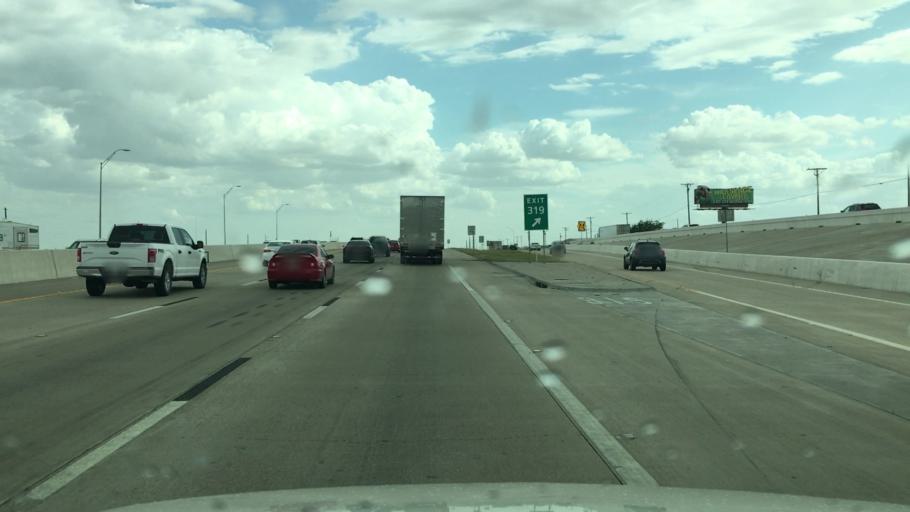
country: US
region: Texas
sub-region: McLennan County
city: Lorena
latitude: 31.3575
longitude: -97.2186
